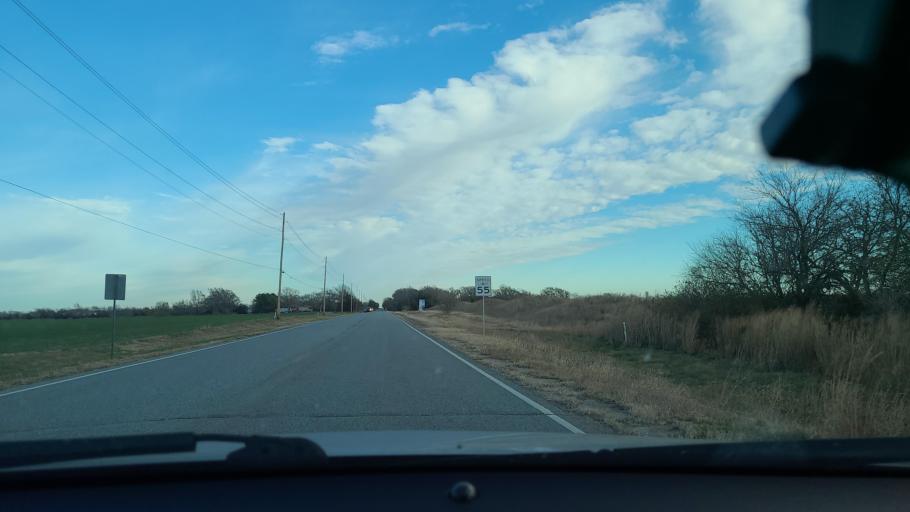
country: US
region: Kansas
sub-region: Sedgwick County
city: Goddard
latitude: 37.6496
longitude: -97.5601
